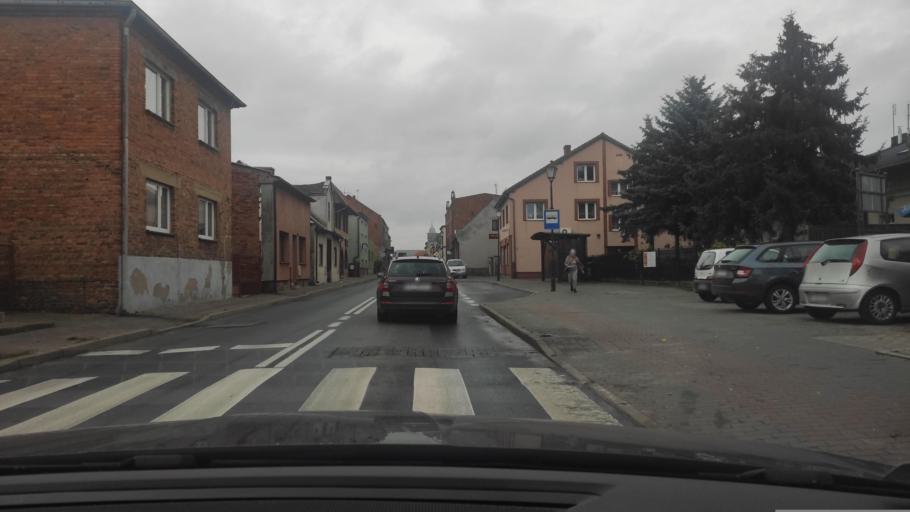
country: PL
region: Greater Poland Voivodeship
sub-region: Powiat poznanski
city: Kostrzyn
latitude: 52.3981
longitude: 17.2240
